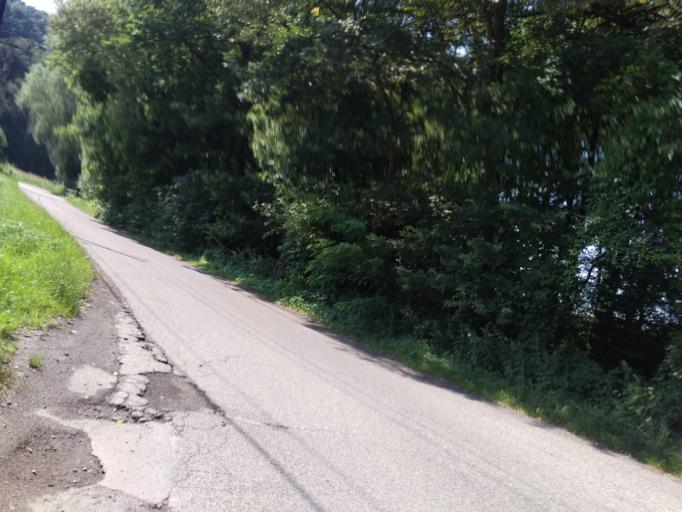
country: AT
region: Styria
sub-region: Politischer Bezirk Graz-Umgebung
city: Werndorf
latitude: 46.9086
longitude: 15.4933
